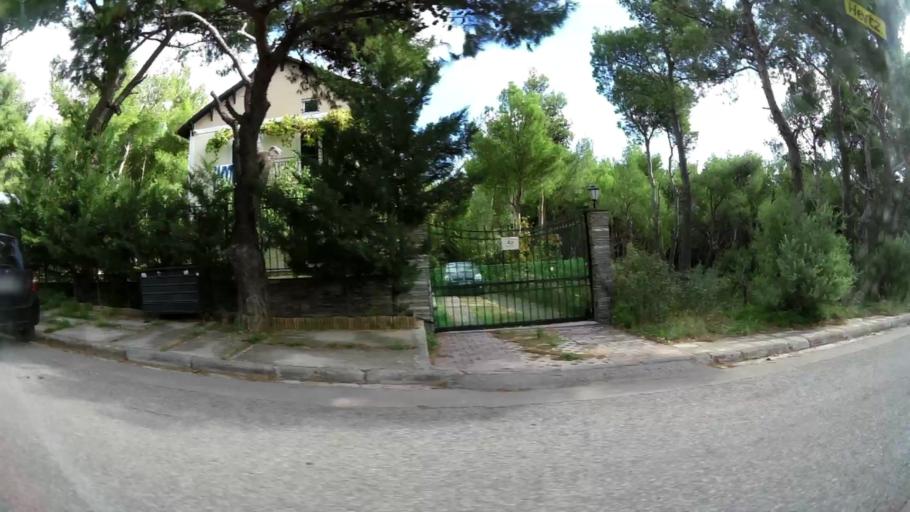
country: GR
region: Attica
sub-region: Nomarchia Anatolikis Attikis
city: Thrakomakedones
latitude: 38.1335
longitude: 23.7623
